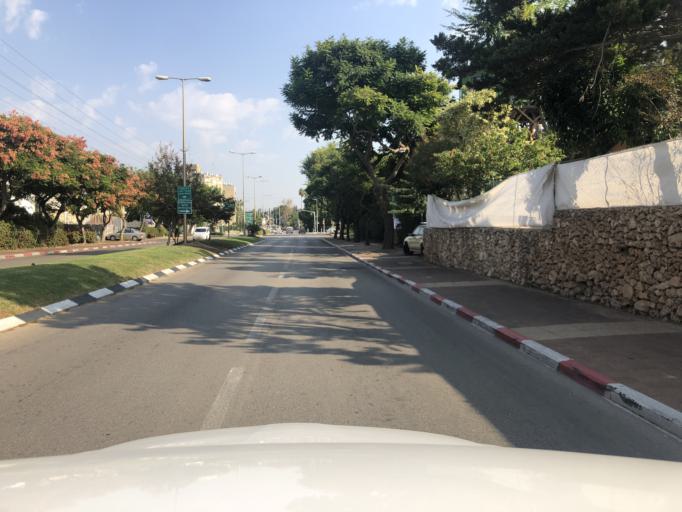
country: IL
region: Central District
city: Kfar Saba
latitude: 32.1858
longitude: 34.9028
